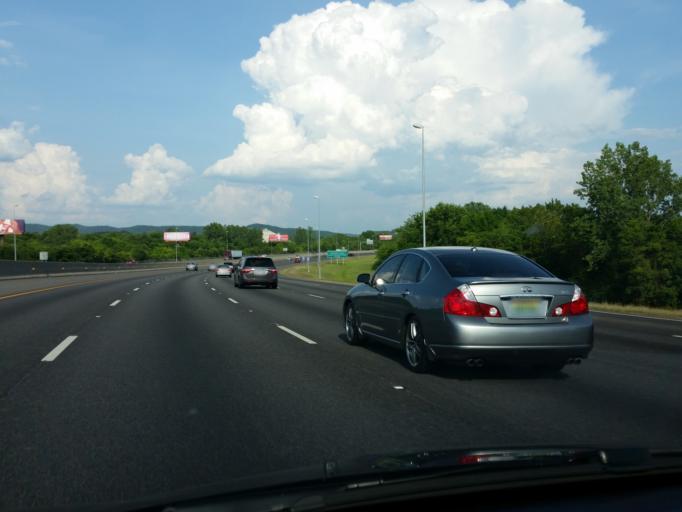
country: US
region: Alabama
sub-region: Jefferson County
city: Tarrant
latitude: 33.5502
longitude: -86.7729
